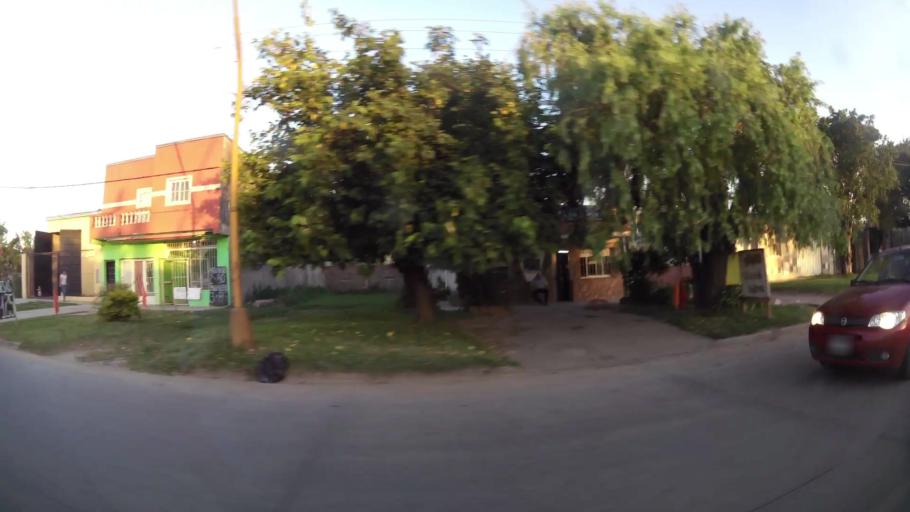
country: AR
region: Santa Fe
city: Santa Fe de la Vera Cruz
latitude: -31.5932
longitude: -60.6992
